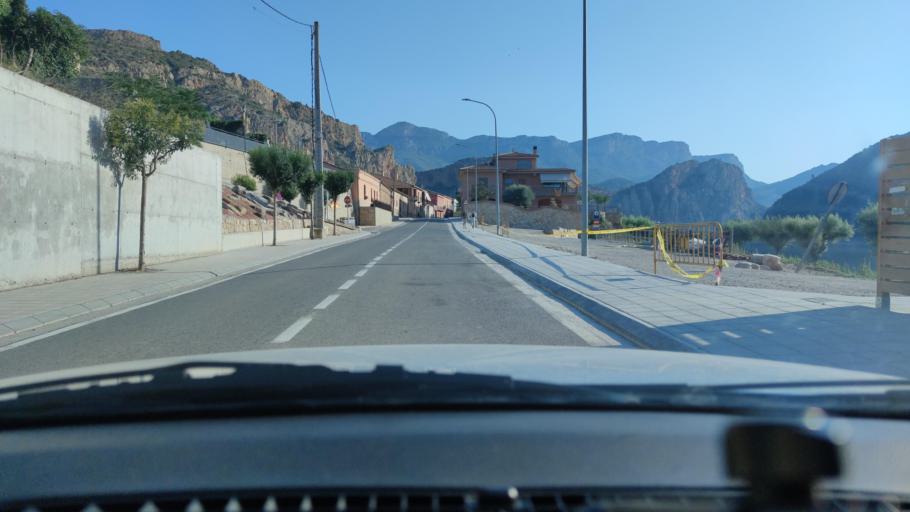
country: ES
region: Catalonia
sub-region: Provincia de Lleida
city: Camarasa
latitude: 41.8663
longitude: 0.8405
